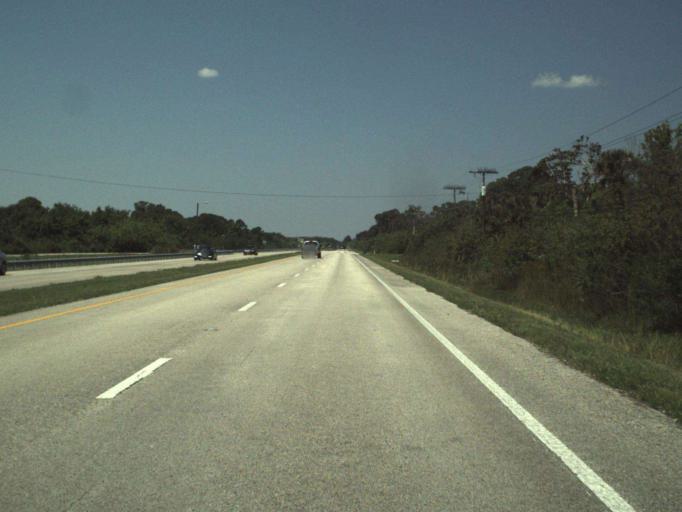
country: US
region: Florida
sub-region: Brevard County
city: Merritt Island
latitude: 28.4789
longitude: -80.6900
